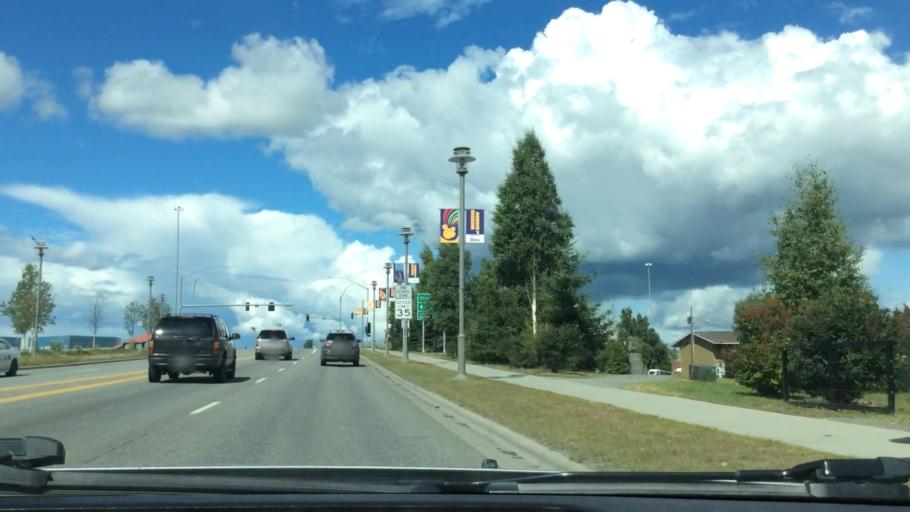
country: US
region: Alaska
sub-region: Anchorage Municipality
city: Anchorage
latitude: 61.2192
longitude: -149.8083
